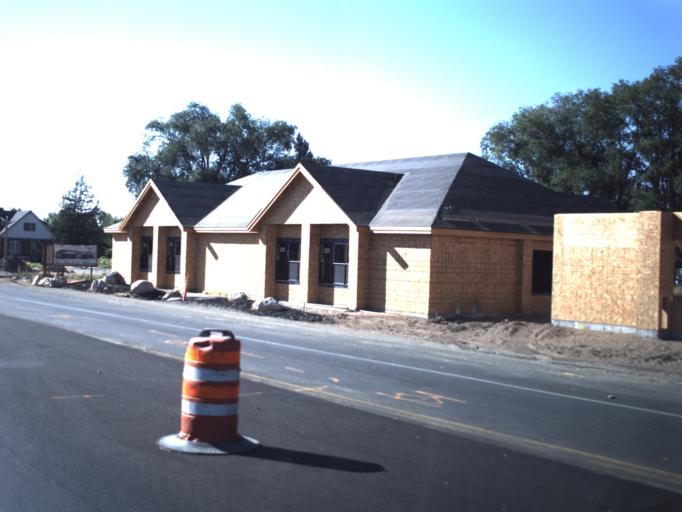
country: US
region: Utah
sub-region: Weber County
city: Hooper
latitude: 41.1908
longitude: -112.1019
